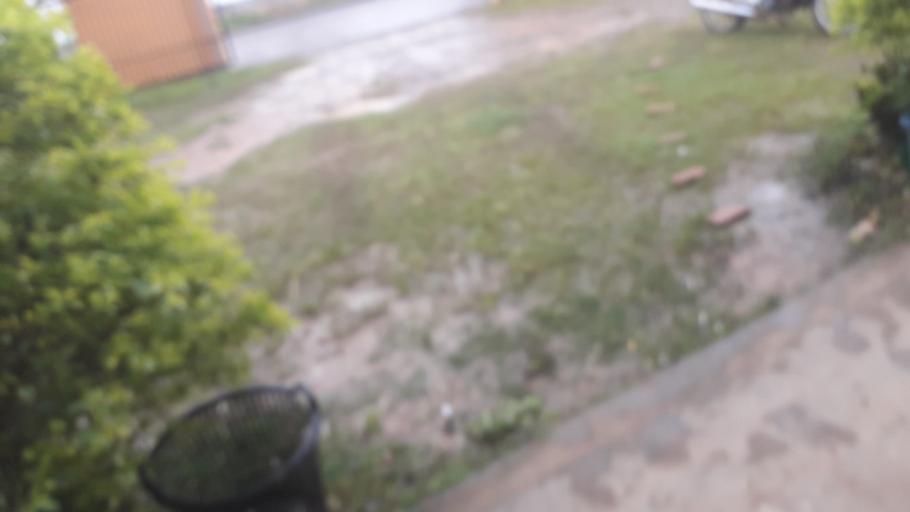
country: LA
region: Loungnamtha
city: Muang Nale
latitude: 20.1480
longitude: 101.4662
